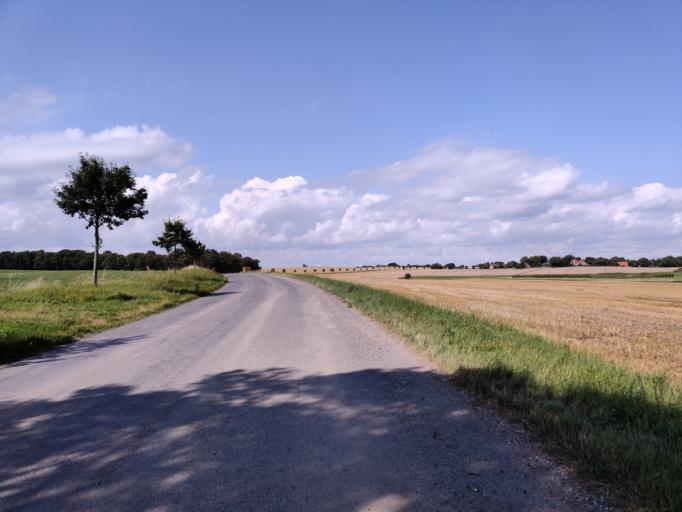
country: DK
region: Zealand
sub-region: Guldborgsund Kommune
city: Nykobing Falster
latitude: 54.6460
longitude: 11.8920
